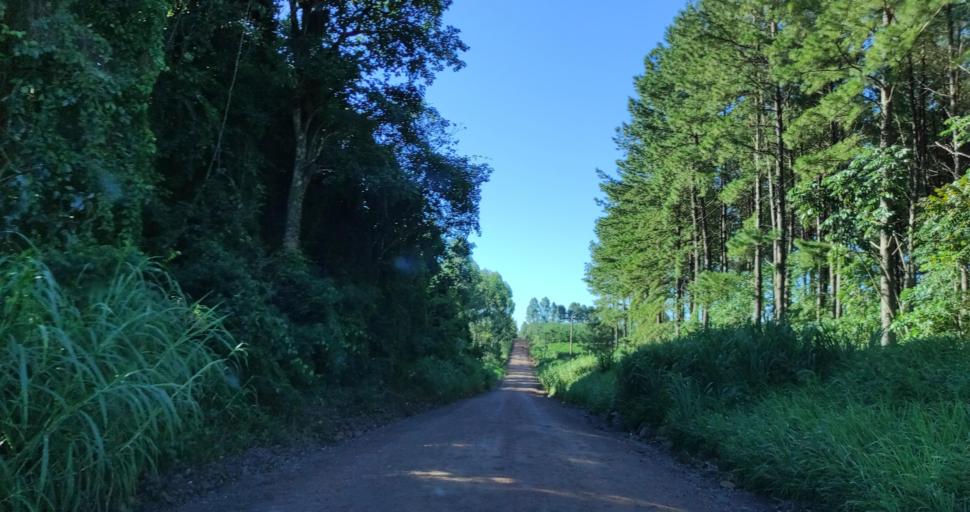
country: AR
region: Misiones
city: Garuhape
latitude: -26.8846
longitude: -54.9967
